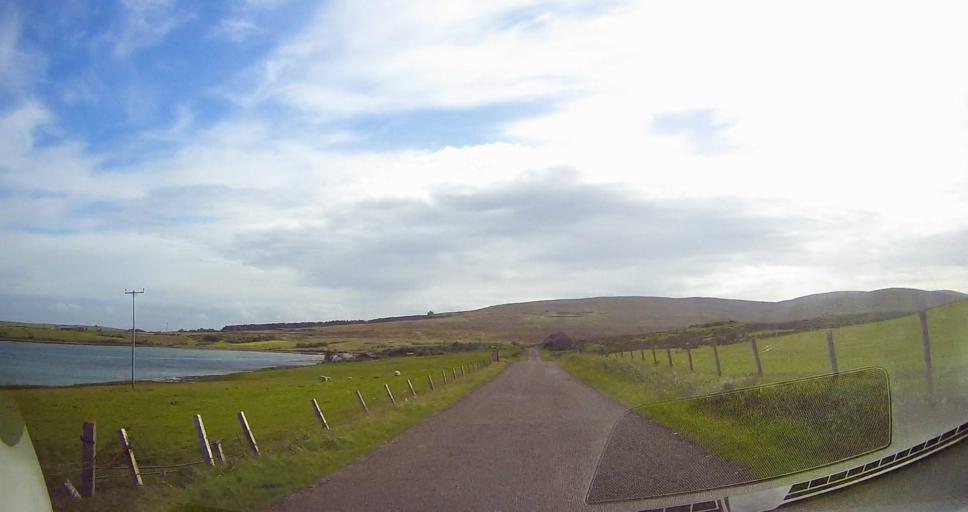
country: GB
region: Scotland
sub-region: Orkney Islands
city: Stromness
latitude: 58.8454
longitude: -3.2084
